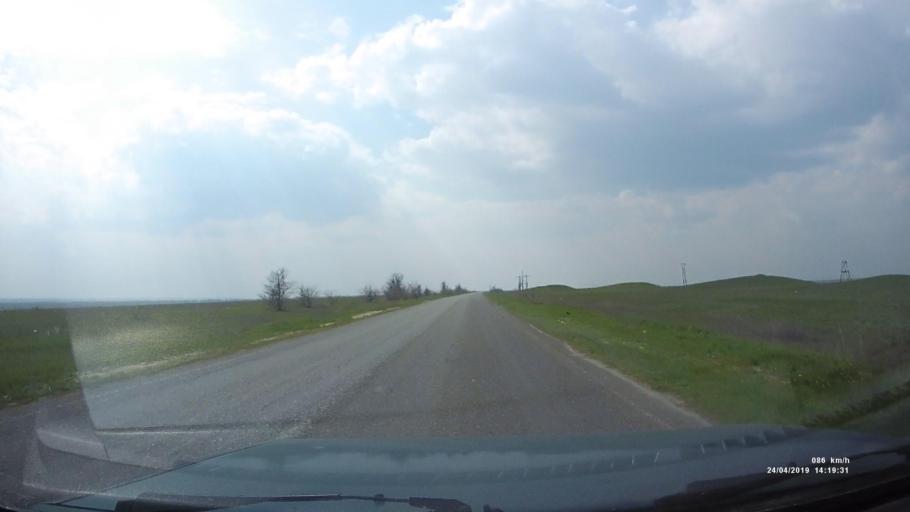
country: RU
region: Kalmykiya
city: Arshan'
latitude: 46.3057
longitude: 44.1742
